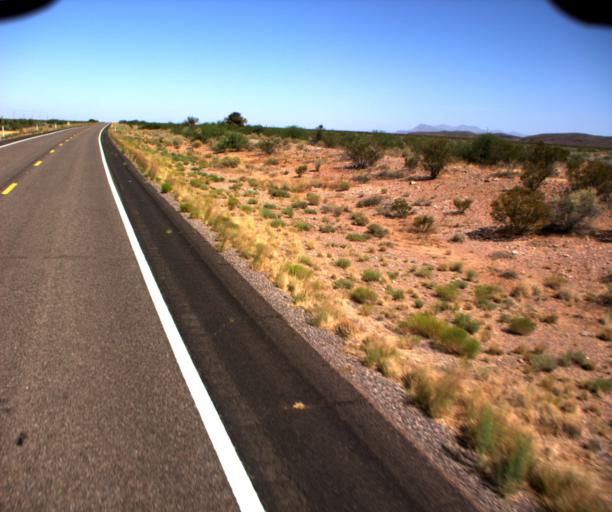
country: US
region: Arizona
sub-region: Graham County
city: Swift Trail Junction
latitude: 32.7544
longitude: -109.4190
